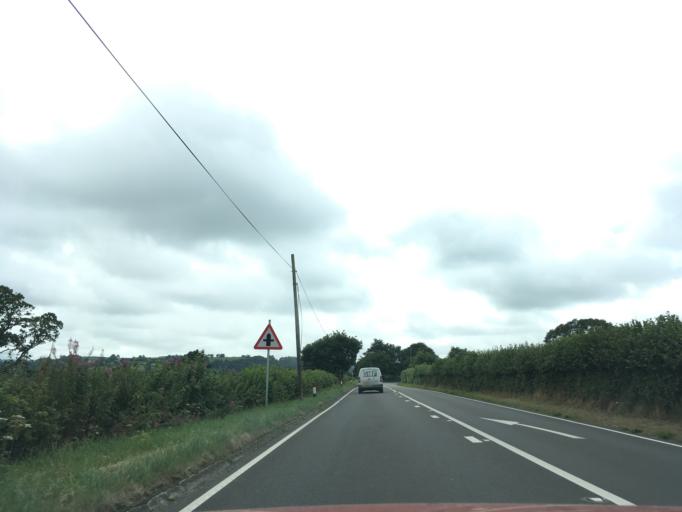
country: GB
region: Wales
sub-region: Carmarthenshire
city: Llanfynydd
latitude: 51.8715
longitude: -4.1183
